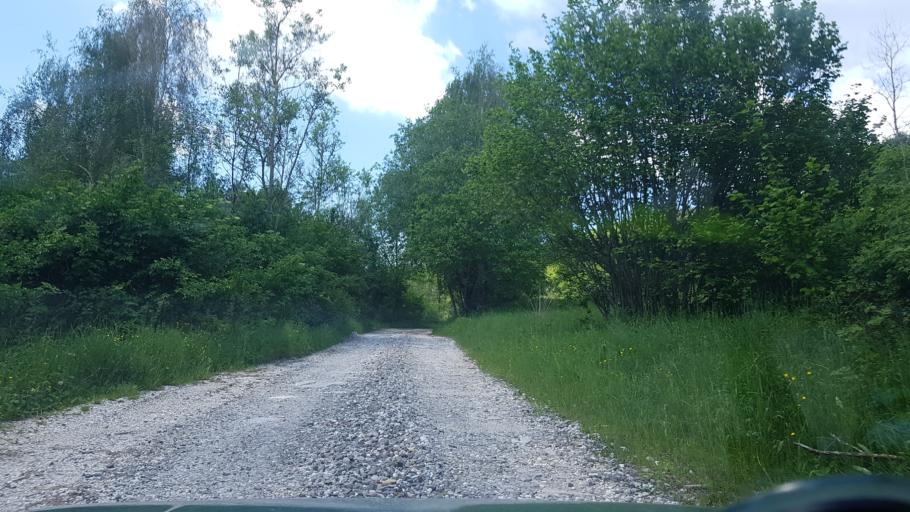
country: IT
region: Friuli Venezia Giulia
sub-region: Provincia di Udine
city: Pulfero
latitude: 46.1813
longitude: 13.4317
